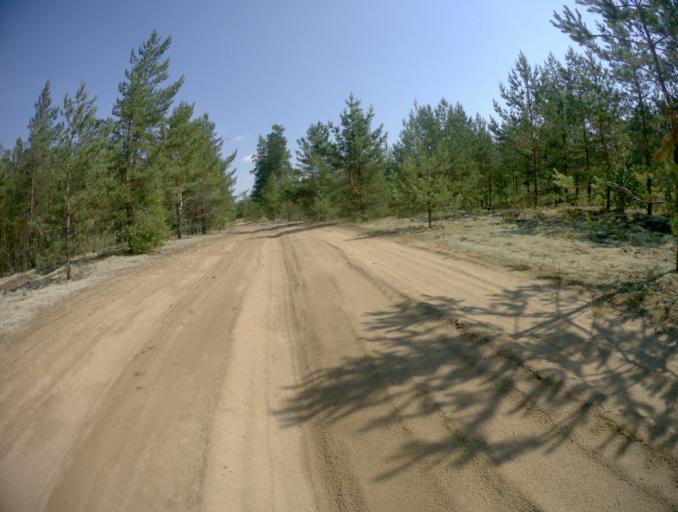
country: RU
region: Ivanovo
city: Talitsy
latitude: 56.3873
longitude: 42.2512
